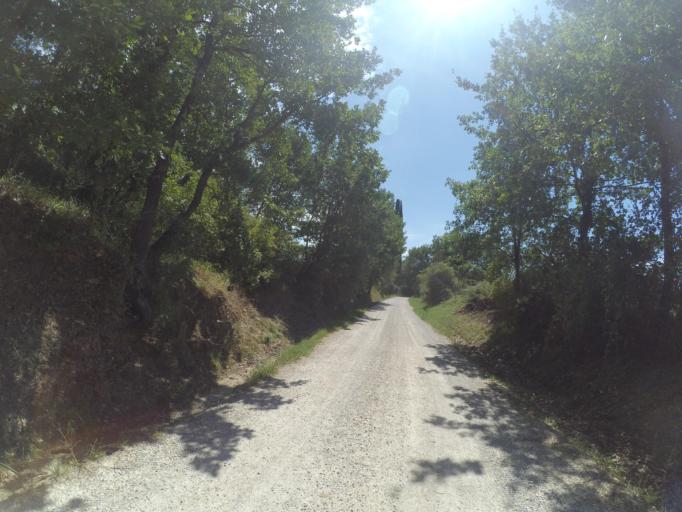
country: IT
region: Tuscany
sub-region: Province of Arezzo
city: Castiglion Fibocchi
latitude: 43.5338
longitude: 11.7654
